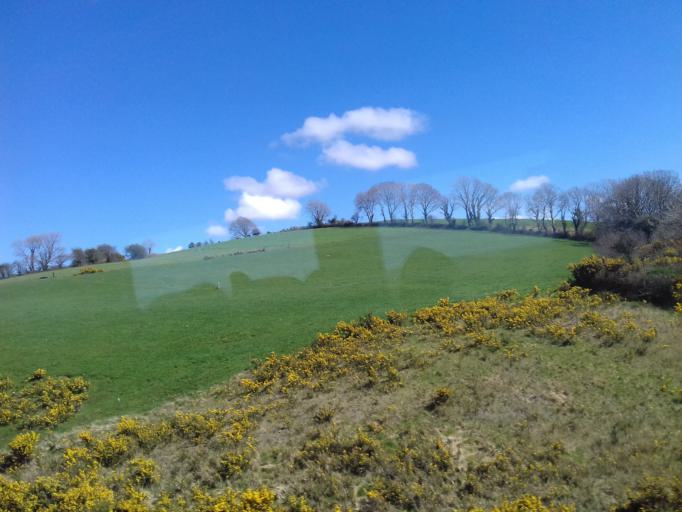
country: IE
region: Munster
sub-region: Ciarrai
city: Castleisland
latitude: 52.1662
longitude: -9.5778
